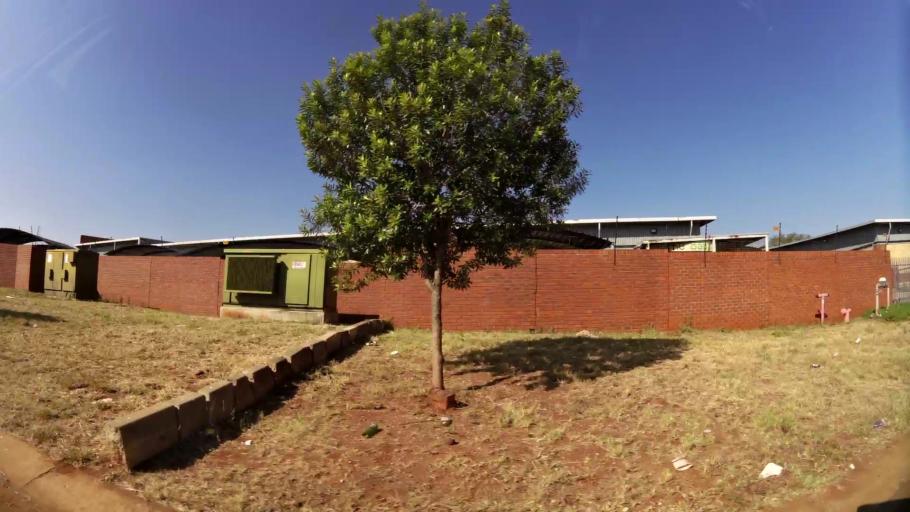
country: ZA
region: Gauteng
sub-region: City of Tshwane Metropolitan Municipality
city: Pretoria
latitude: -25.6792
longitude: 28.1915
